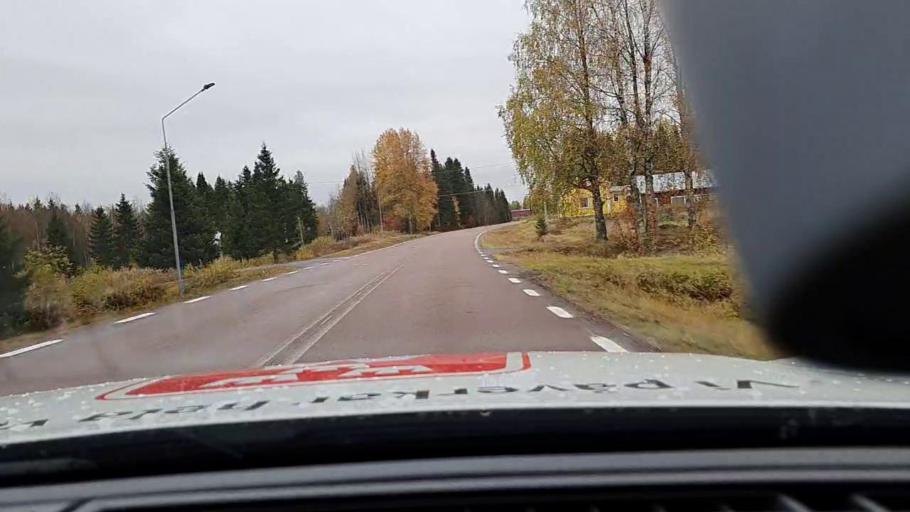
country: FI
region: Lapland
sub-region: Torniolaakso
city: Ylitornio
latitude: 66.1454
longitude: 23.8948
